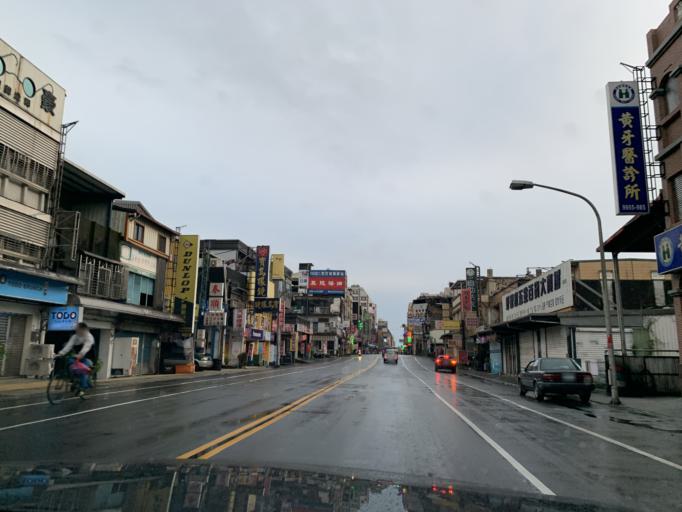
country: TW
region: Taiwan
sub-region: Yilan
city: Yilan
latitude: 24.5959
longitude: 121.8480
